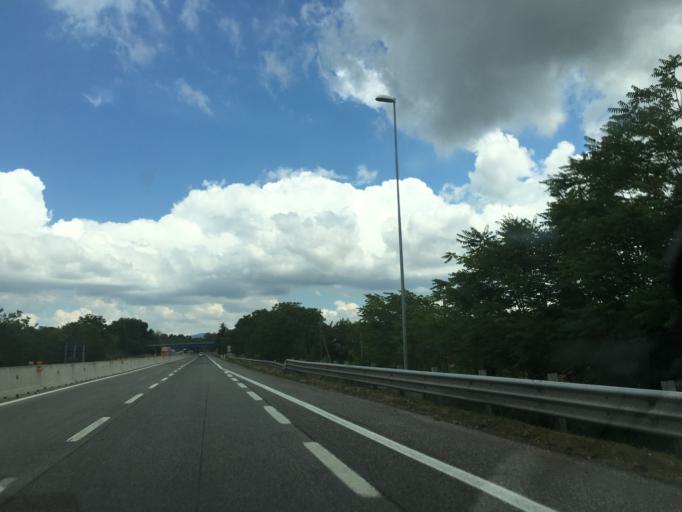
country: IT
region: Campania
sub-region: Provincia di Avellino
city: Passo di Mirabella-Pianopantano
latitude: 41.0599
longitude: 15.0168
